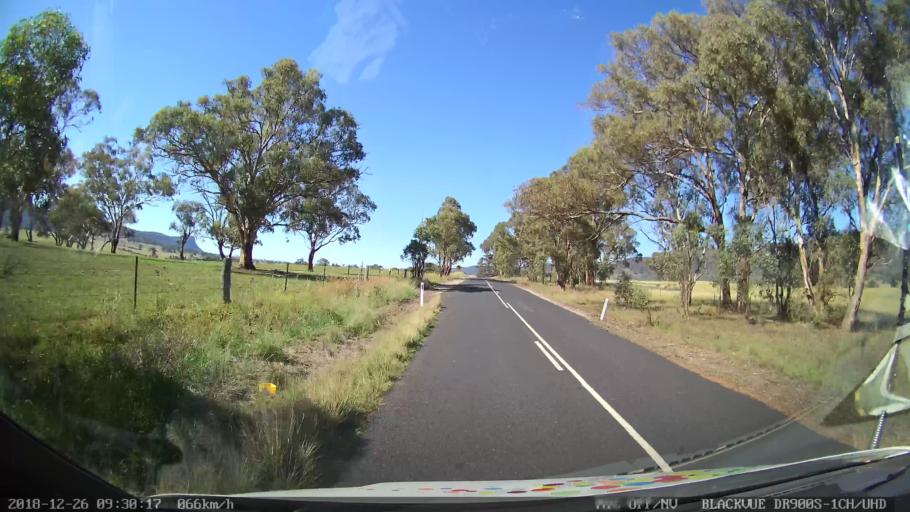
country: AU
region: New South Wales
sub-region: Mid-Western Regional
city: Kandos
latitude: -32.8614
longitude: 150.0298
